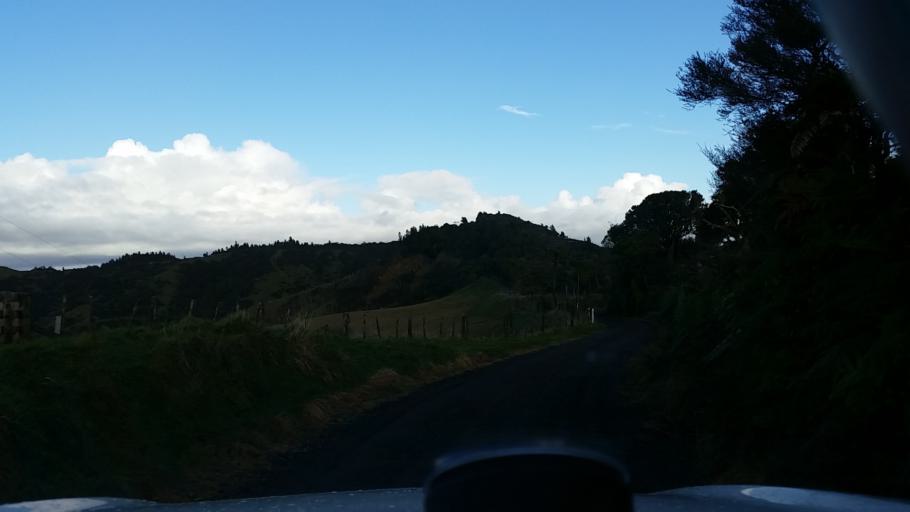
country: NZ
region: Taranaki
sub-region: South Taranaki District
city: Eltham
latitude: -39.4131
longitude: 174.5660
